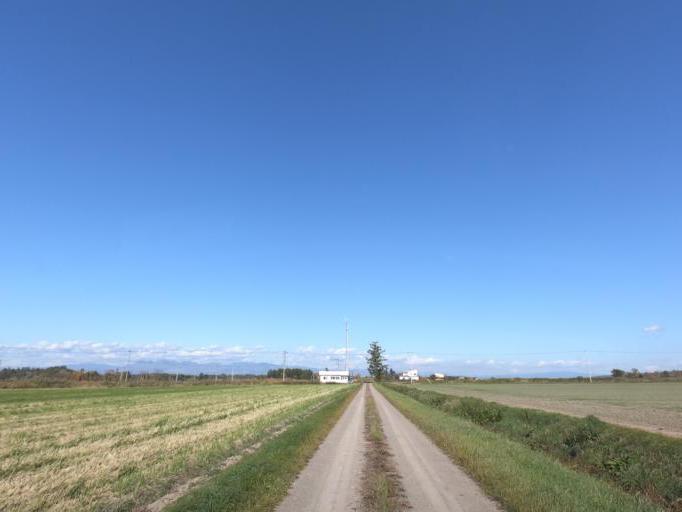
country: JP
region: Hokkaido
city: Otofuke
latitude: 43.0360
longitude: 143.2725
